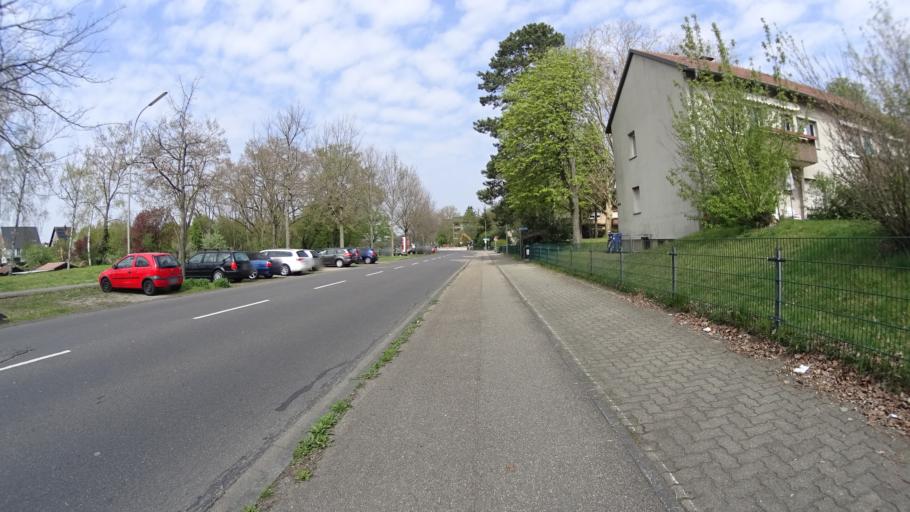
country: DE
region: Baden-Wuerttemberg
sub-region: Karlsruhe Region
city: Karlsruhe
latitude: 49.0313
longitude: 8.3651
